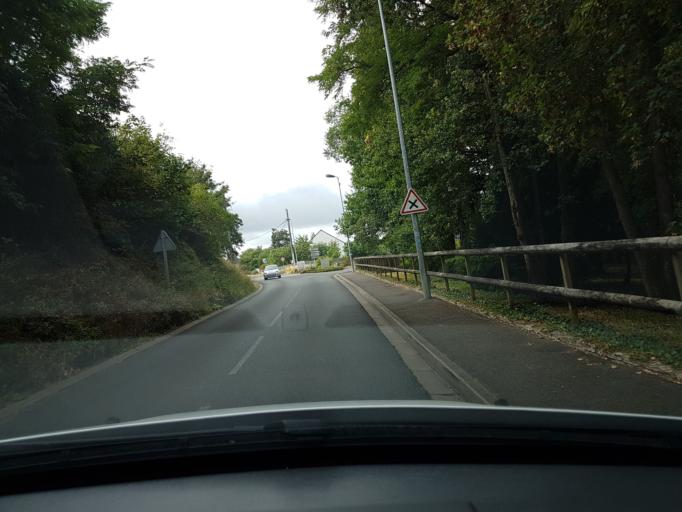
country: FR
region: Centre
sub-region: Departement d'Indre-et-Loire
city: Larcay
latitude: 47.3653
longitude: 0.7804
